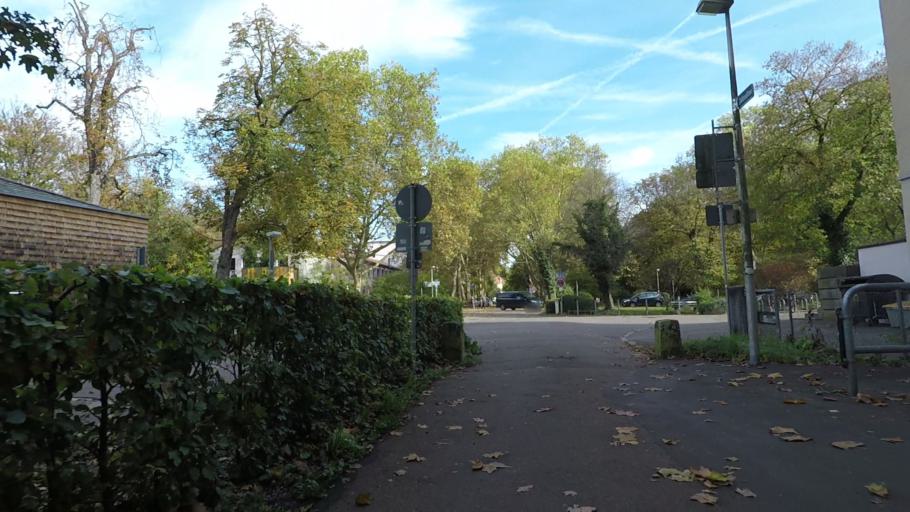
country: DE
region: Baden-Wuerttemberg
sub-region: Tuebingen Region
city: Tuebingen
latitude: 48.5133
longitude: 9.0437
